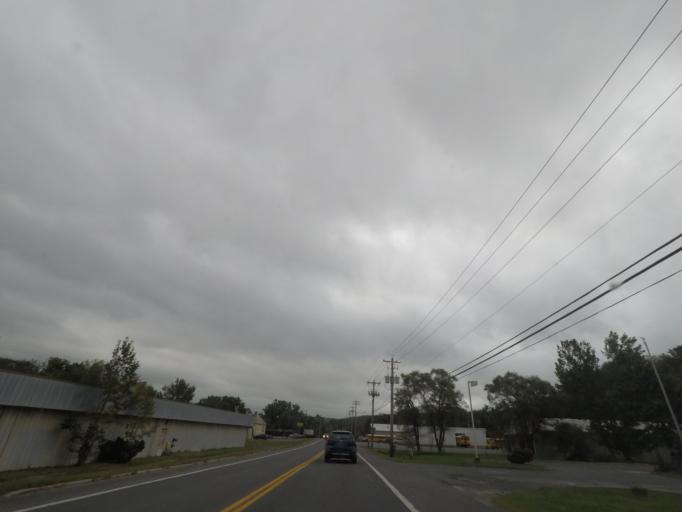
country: US
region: New York
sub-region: Rensselaer County
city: Hoosick Falls
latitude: 42.8914
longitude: -73.3607
